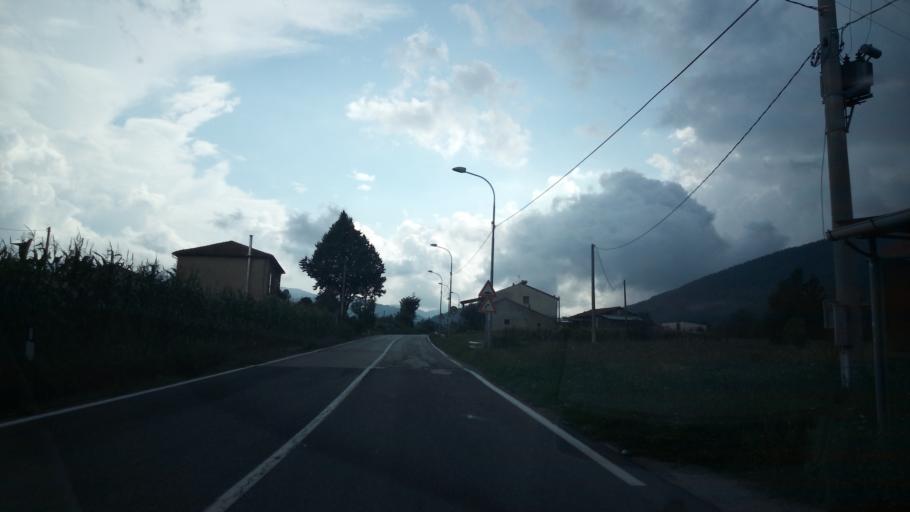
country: IT
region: Campania
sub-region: Provincia di Salerno
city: Buonabitacolo
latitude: 40.2836
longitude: 15.6345
